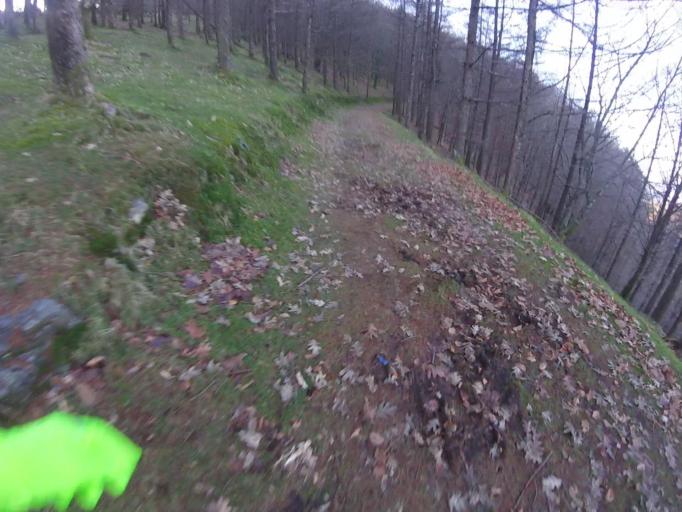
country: ES
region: Basque Country
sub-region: Provincia de Guipuzcoa
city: Irun
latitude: 43.2944
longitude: -1.7863
